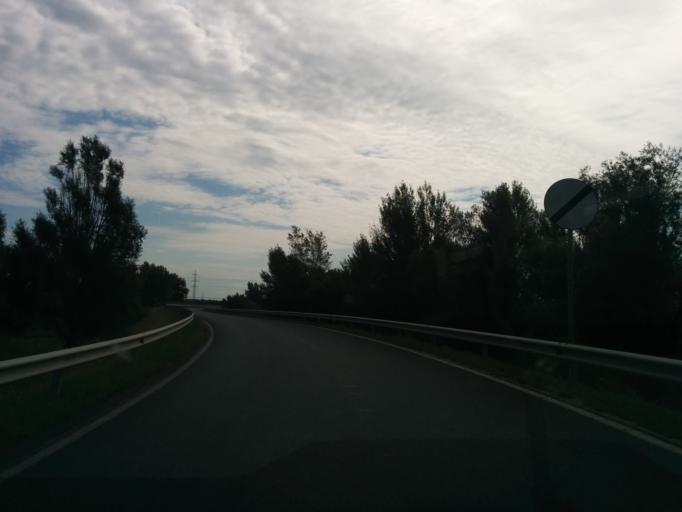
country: HU
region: Gyor-Moson-Sopron
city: Abda
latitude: 47.6753
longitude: 17.5497
